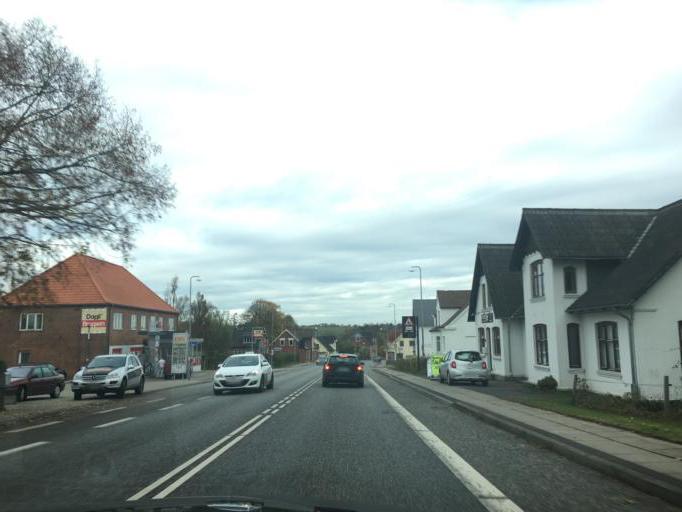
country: DK
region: South Denmark
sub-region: Vejle Kommune
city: Vejle
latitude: 55.6556
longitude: 9.5053
